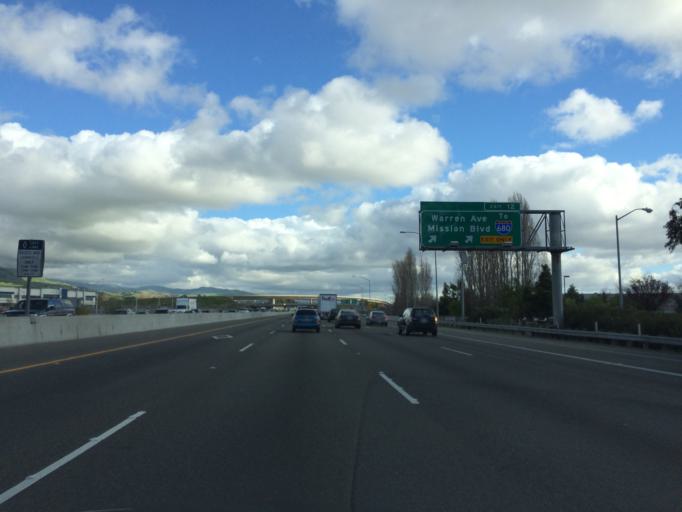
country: US
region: California
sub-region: Santa Clara County
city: Milpitas
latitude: 37.4883
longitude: -121.9430
